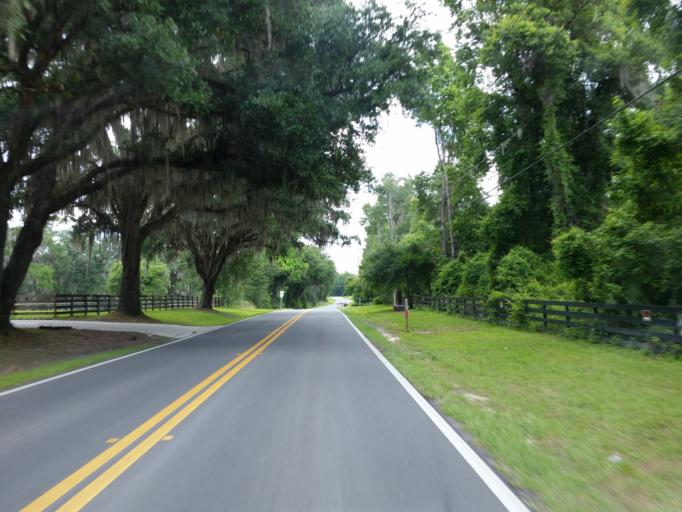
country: US
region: Florida
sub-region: Hernando County
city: North Brooksville
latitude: 28.6445
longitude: -82.3597
